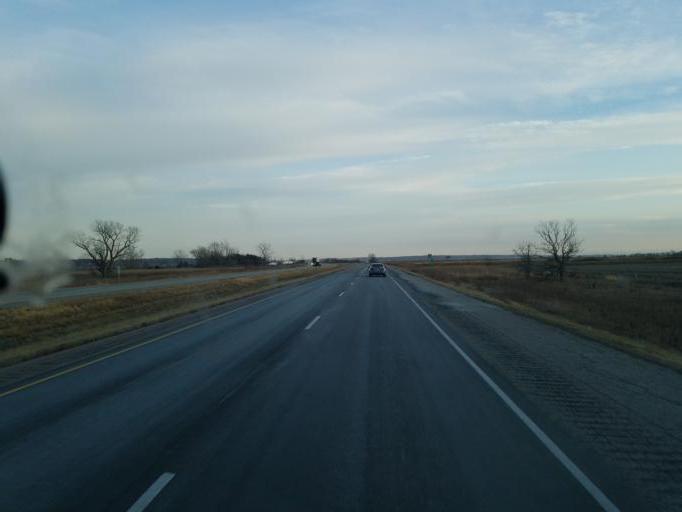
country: US
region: Iowa
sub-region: Harrison County
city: Missouri Valley
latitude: 41.5881
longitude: -95.9486
